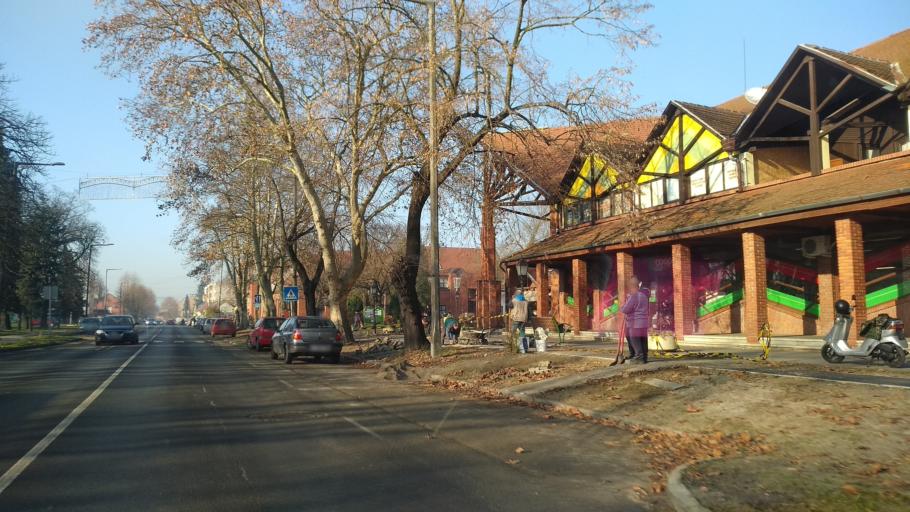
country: HU
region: Somogy
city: Barcs
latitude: 45.9592
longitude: 17.4648
